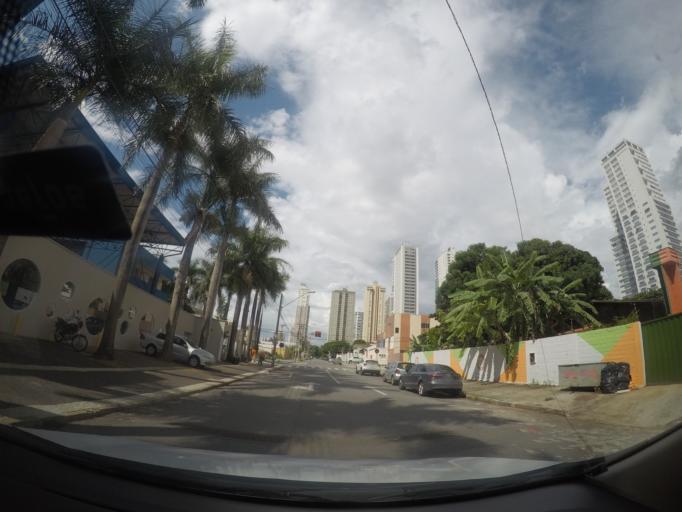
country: BR
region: Goias
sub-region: Goiania
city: Goiania
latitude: -16.7047
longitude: -49.2729
